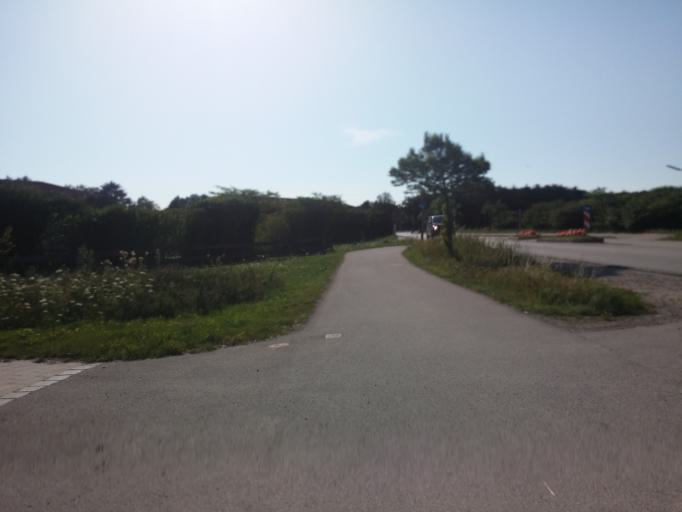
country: DE
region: Bavaria
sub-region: Upper Bavaria
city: Feldkirchen
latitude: 48.1305
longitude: 11.7220
